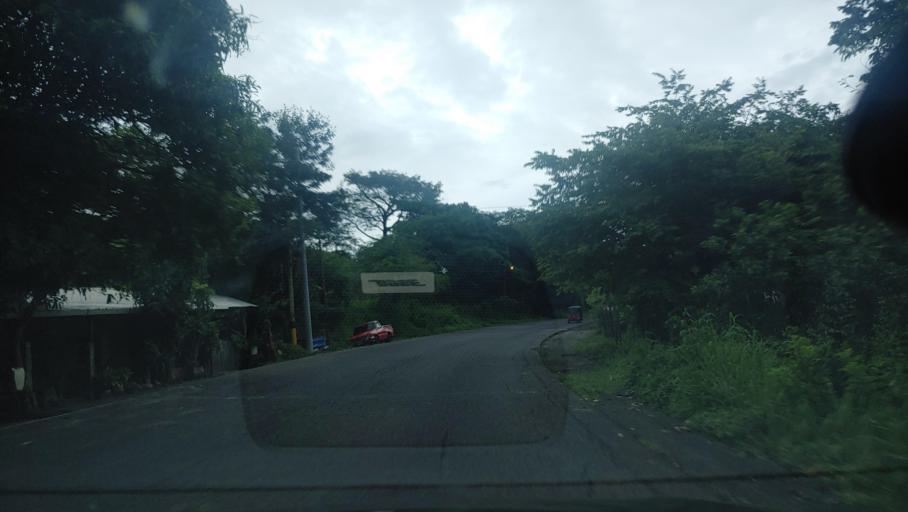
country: HN
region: Choluteca
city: Corpus
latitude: 13.3711
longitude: -87.0009
